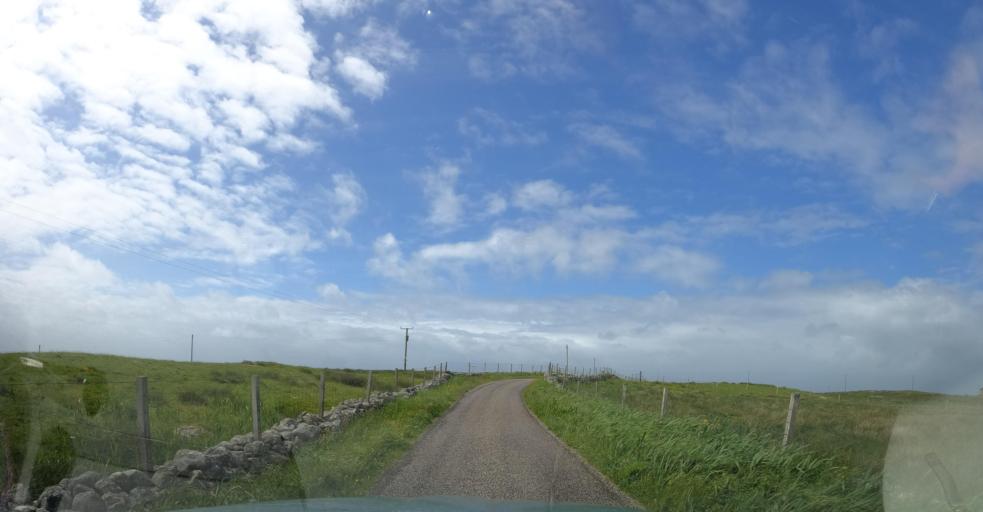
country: GB
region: Scotland
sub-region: Eilean Siar
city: Isle of South Uist
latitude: 57.2738
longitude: -7.4063
